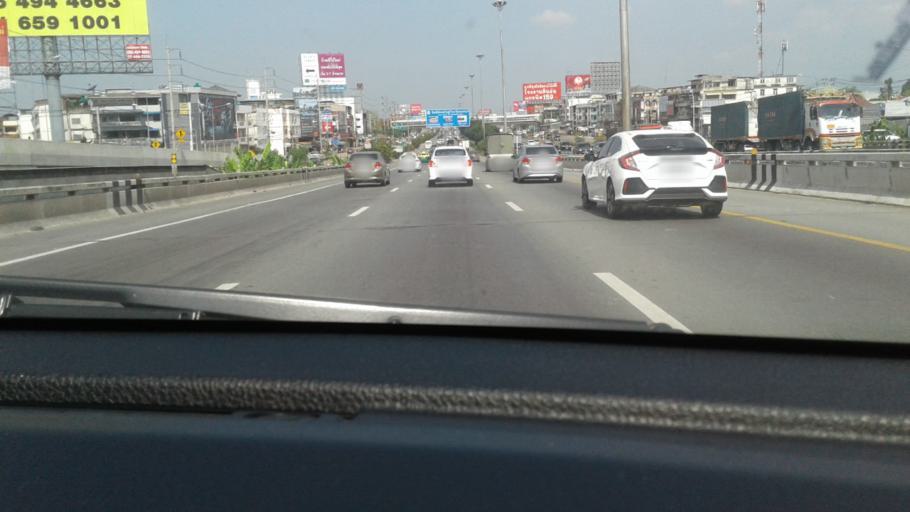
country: TH
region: Bangkok
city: Taling Chan
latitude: 13.8015
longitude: 100.4106
